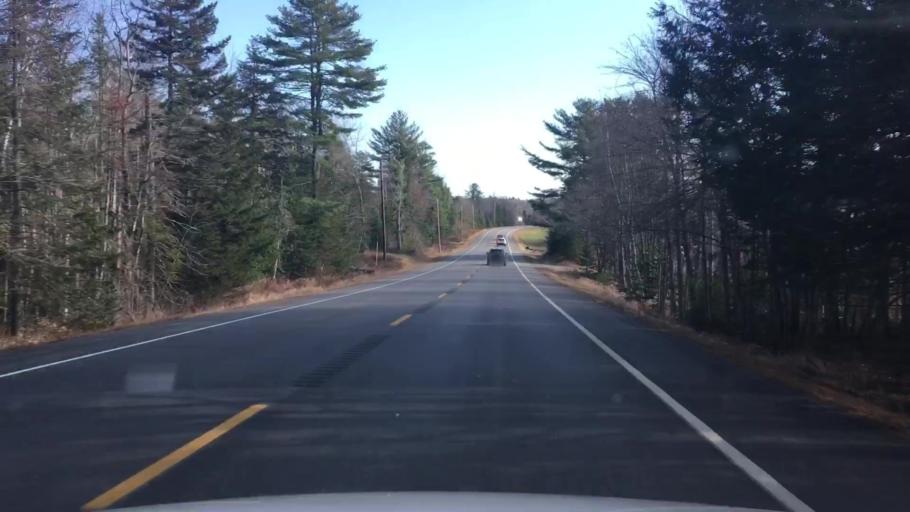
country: US
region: Maine
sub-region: Lincoln County
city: Jefferson
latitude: 44.2541
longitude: -69.4363
